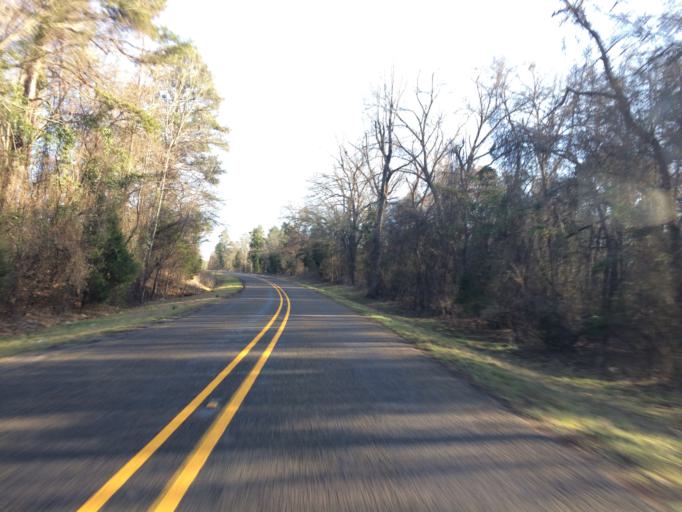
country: US
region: Texas
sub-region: Wood County
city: Mineola
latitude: 32.6917
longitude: -95.3460
